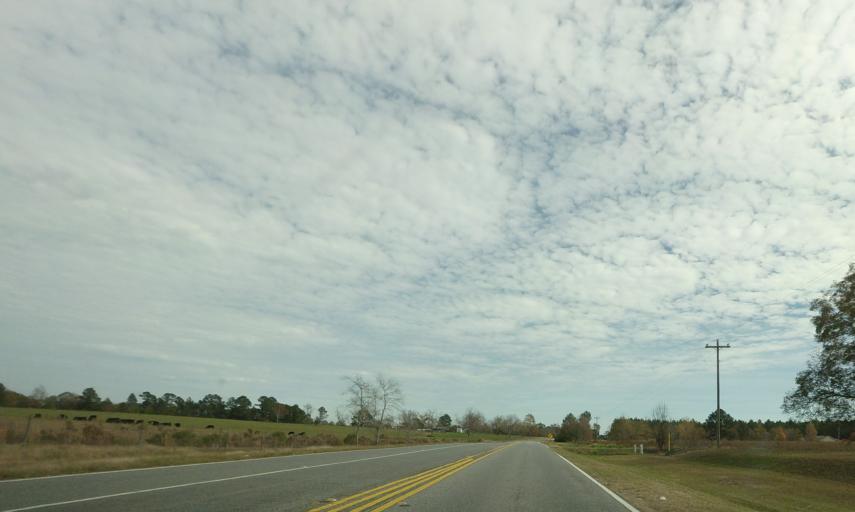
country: US
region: Georgia
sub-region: Bleckley County
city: Cochran
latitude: 32.3976
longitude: -83.3264
